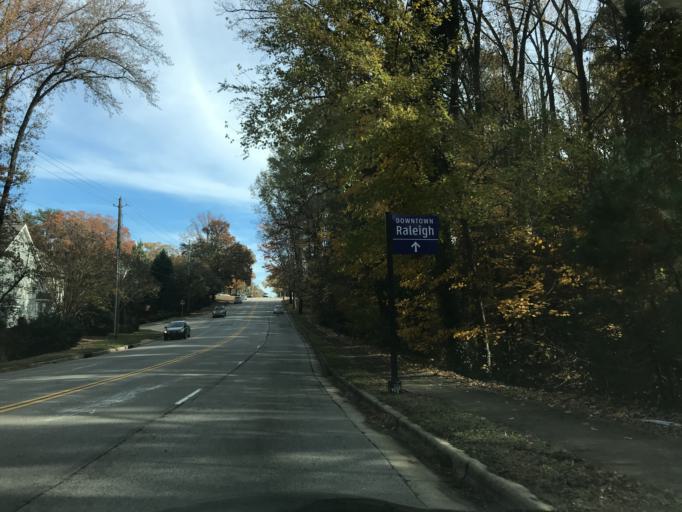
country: US
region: North Carolina
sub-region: Wake County
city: West Raleigh
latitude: 35.8004
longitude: -78.6667
